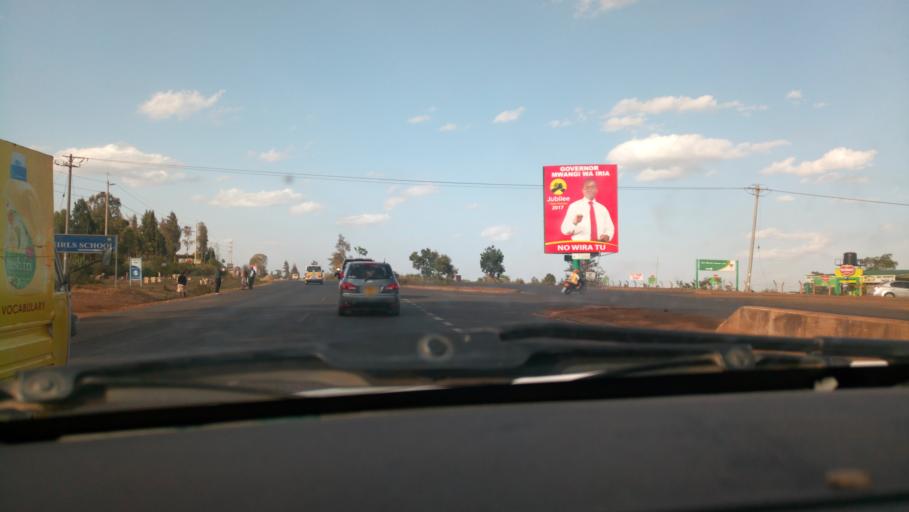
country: KE
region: Nairobi Area
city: Thika
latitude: -1.0199
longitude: 37.0704
